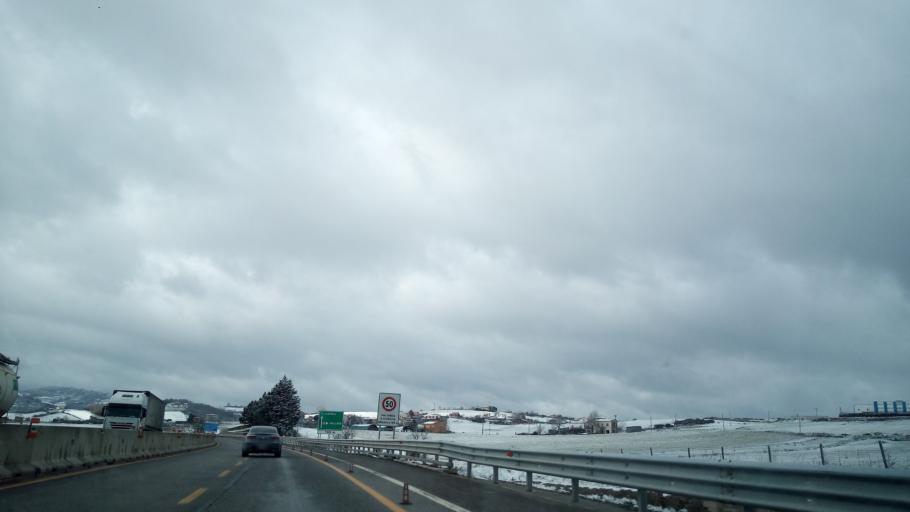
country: IT
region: Campania
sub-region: Provincia di Avellino
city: Scampitella
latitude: 41.0621
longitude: 15.3015
